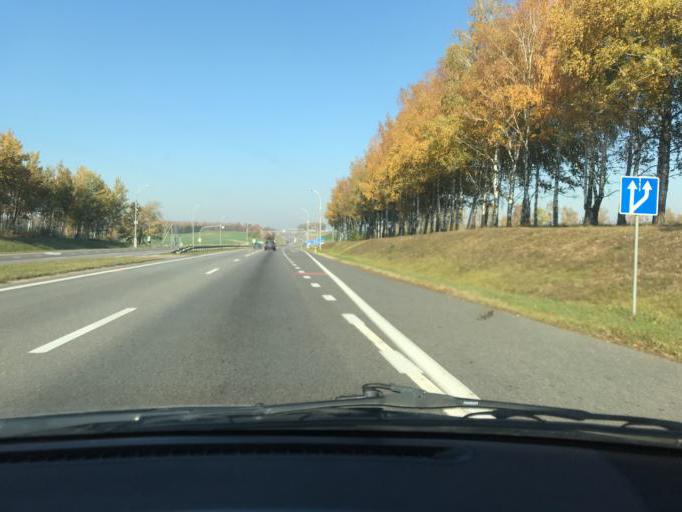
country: BY
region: Minsk
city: Samakhvalavichy
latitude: 53.7166
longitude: 27.5191
